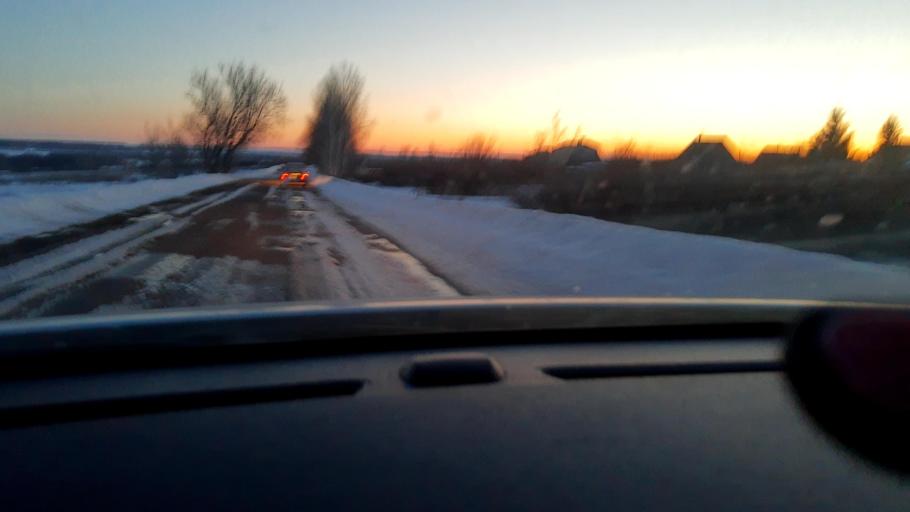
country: RU
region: Bashkortostan
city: Avdon
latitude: 54.3950
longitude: 55.6999
